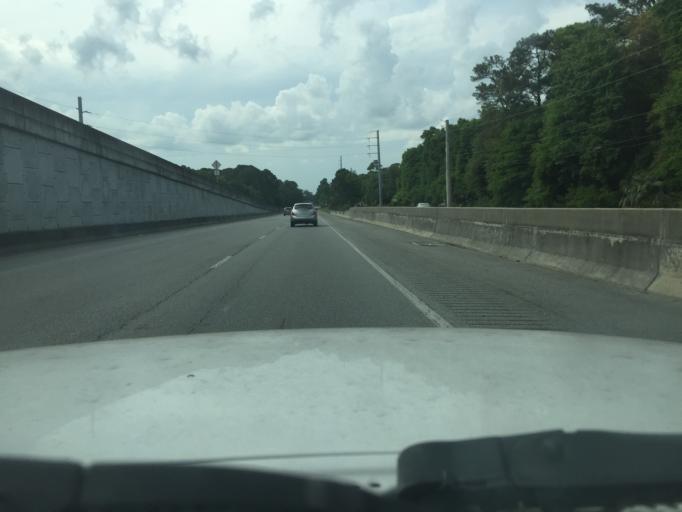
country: US
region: Georgia
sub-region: Chatham County
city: Whitemarsh Island
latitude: 32.0454
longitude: -81.0055
